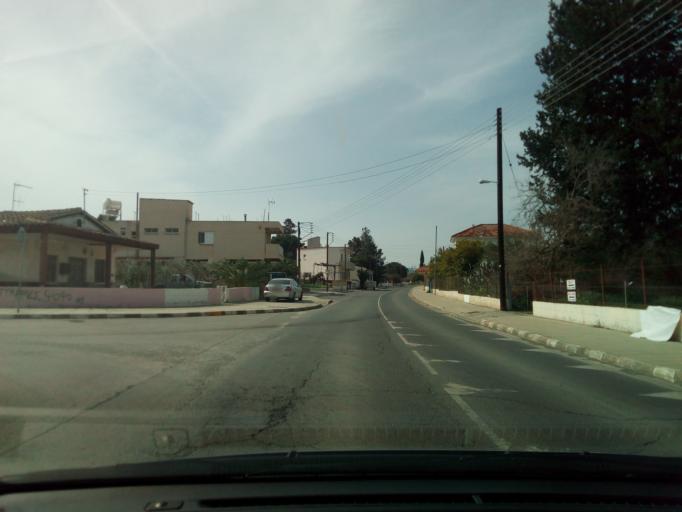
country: CY
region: Lefkosia
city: Pano Deftera
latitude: 35.0825
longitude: 33.2696
